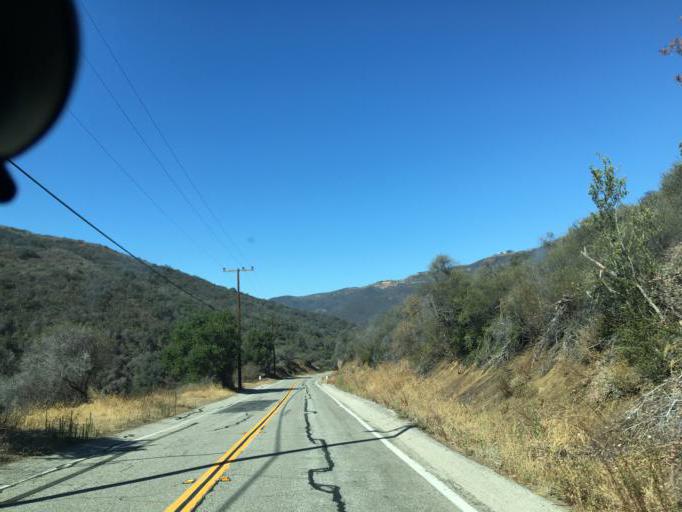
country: US
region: California
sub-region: Ventura County
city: Casa Conejo
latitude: 34.0858
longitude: -118.9088
